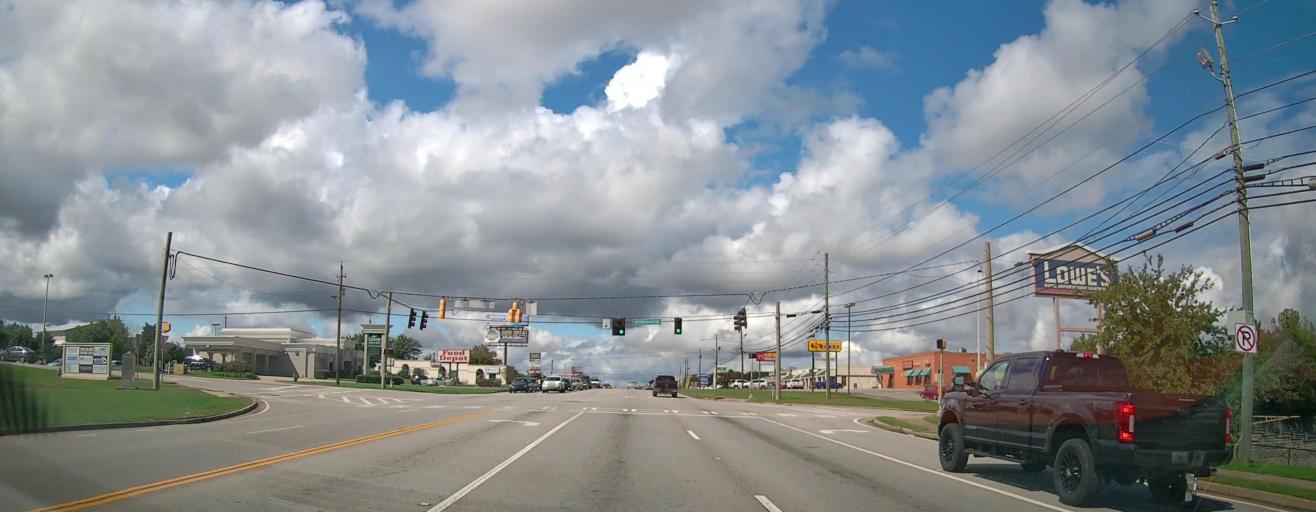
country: US
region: Georgia
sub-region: Baldwin County
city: Milledgeville
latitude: 33.1014
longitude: -83.2480
